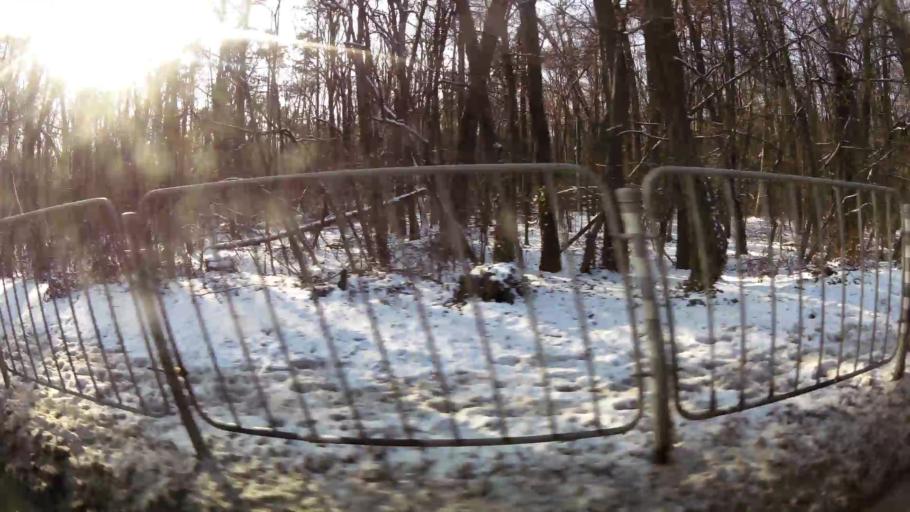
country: BG
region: Sofia-Capital
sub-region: Stolichna Obshtina
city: Sofia
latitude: 42.6705
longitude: 23.3378
